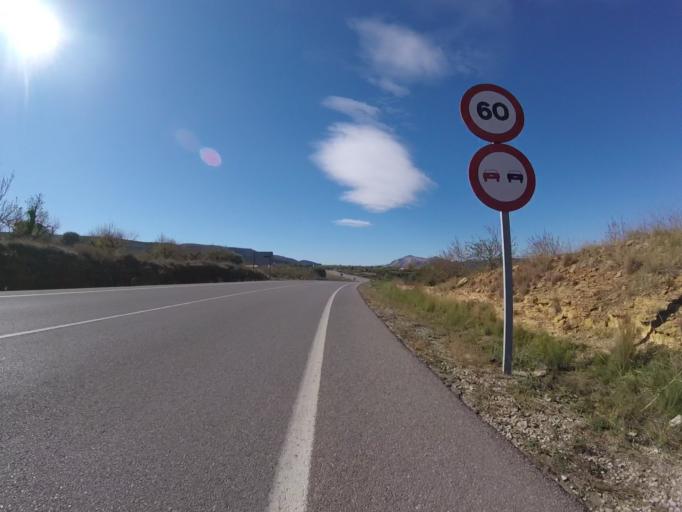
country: ES
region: Valencia
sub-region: Provincia de Castello
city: Albocasser
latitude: 40.3613
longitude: 0.0213
